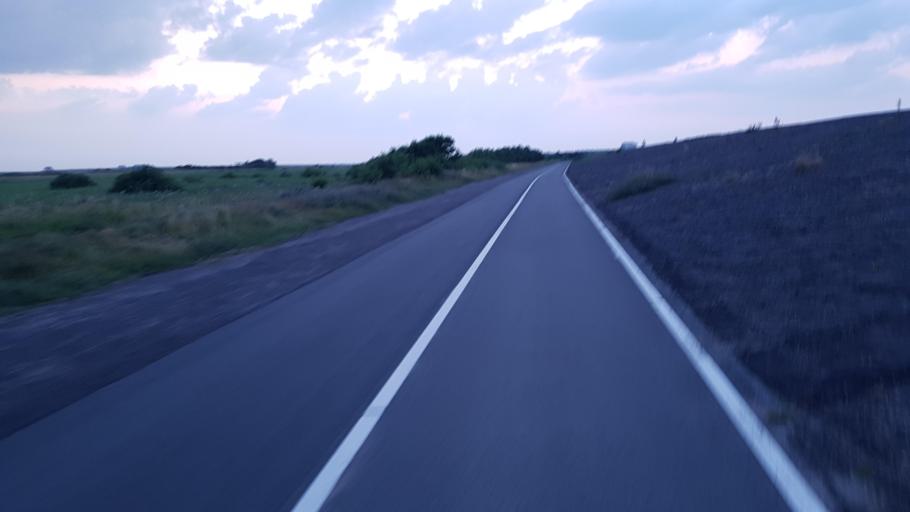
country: DE
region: Schleswig-Holstein
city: Sankt Peter-Ording
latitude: 54.2934
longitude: 8.6413
